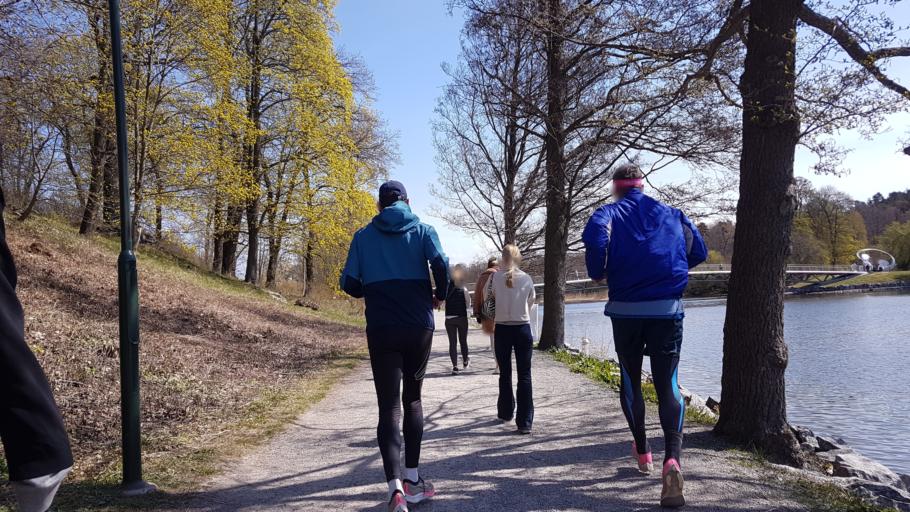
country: SE
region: Stockholm
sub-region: Stockholms Kommun
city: OEstermalm
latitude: 59.3315
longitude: 18.1169
